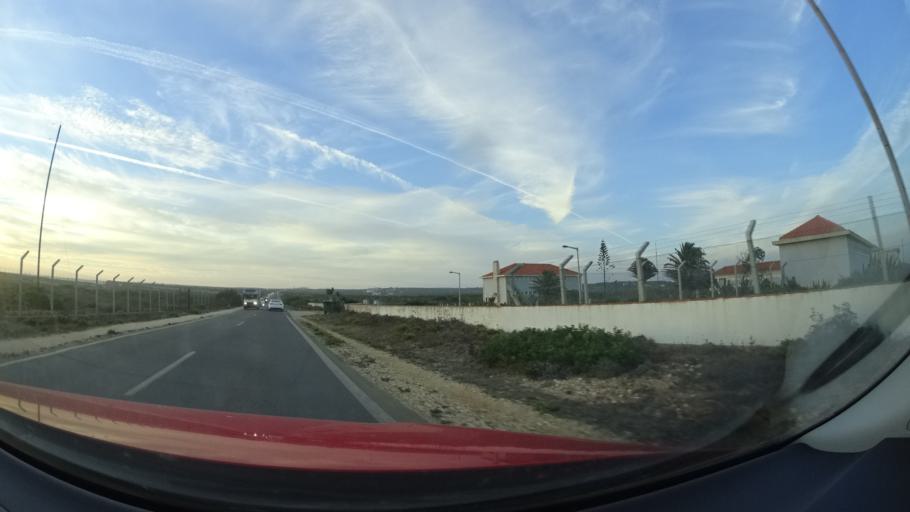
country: PT
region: Faro
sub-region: Vila do Bispo
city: Sagres
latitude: 37.0114
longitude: -8.9508
